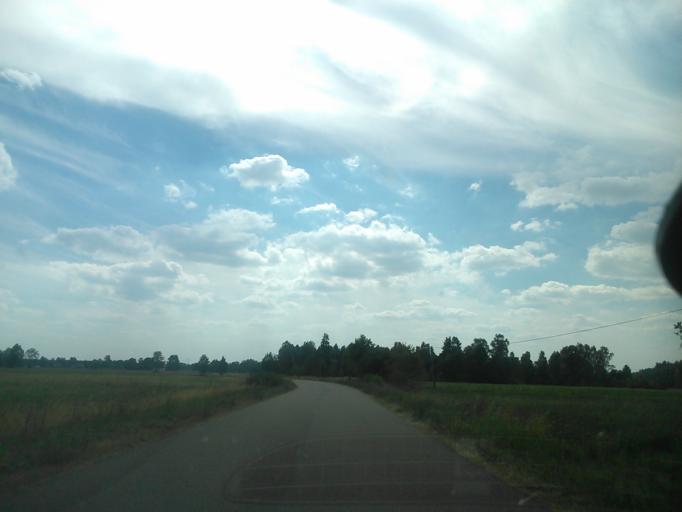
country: PL
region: Masovian Voivodeship
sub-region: Powiat ostrolecki
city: Czarnia
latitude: 53.3761
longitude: 21.1999
